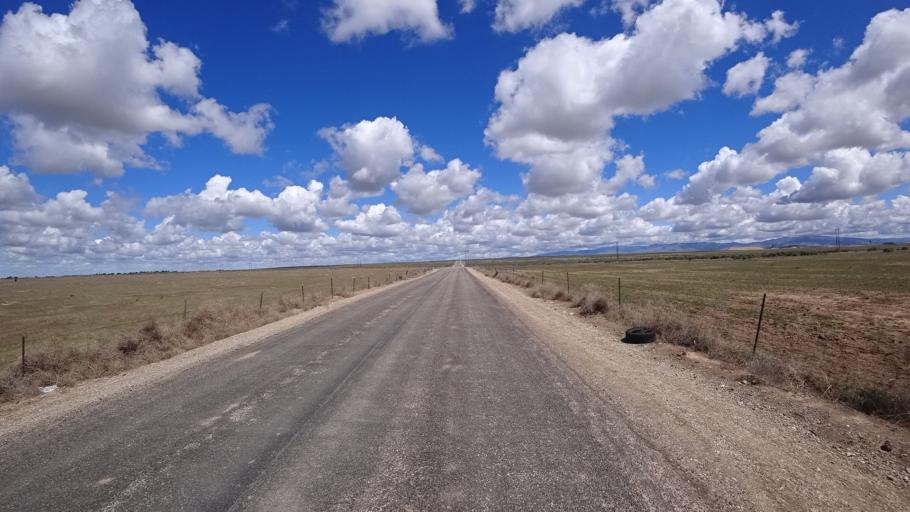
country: US
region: Idaho
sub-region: Ada County
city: Kuna
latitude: 43.4714
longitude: -116.2743
